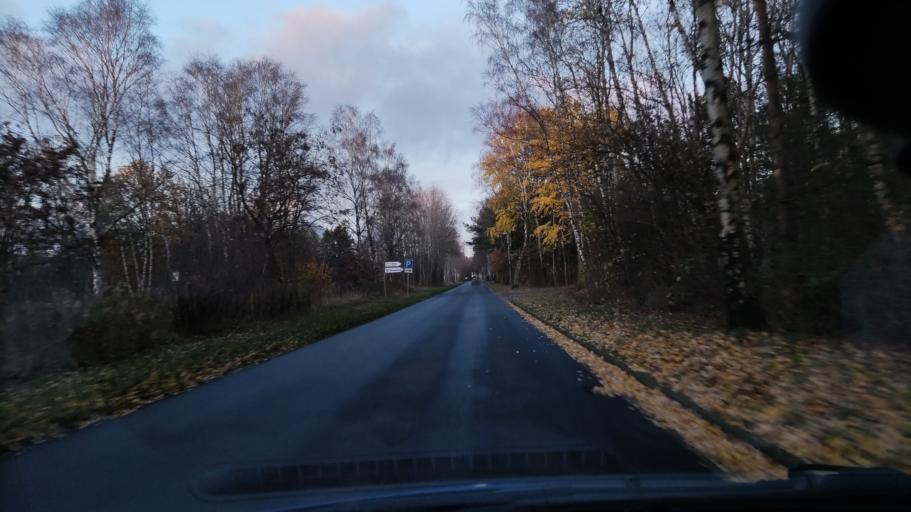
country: DE
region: Lower Saxony
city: Schneverdingen
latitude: 53.1196
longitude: 9.8035
